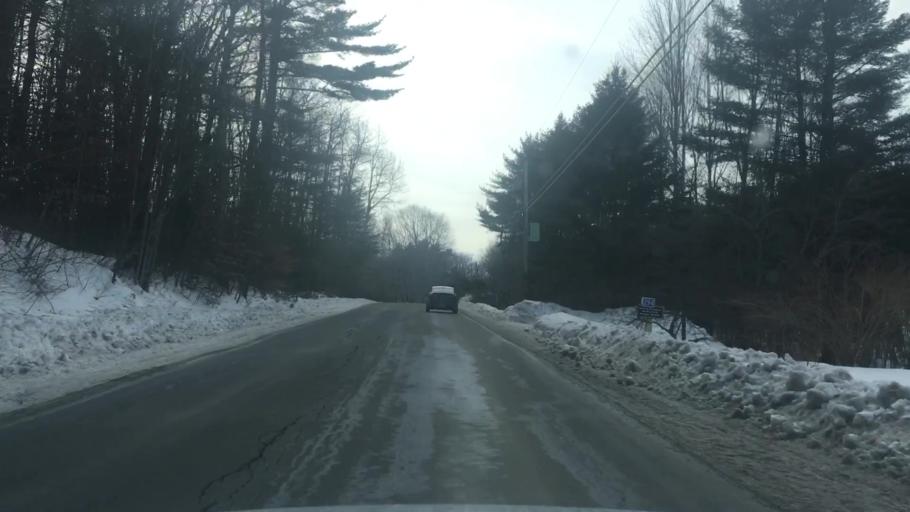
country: US
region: Maine
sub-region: Hancock County
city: Orland
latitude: 44.6151
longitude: -68.7101
